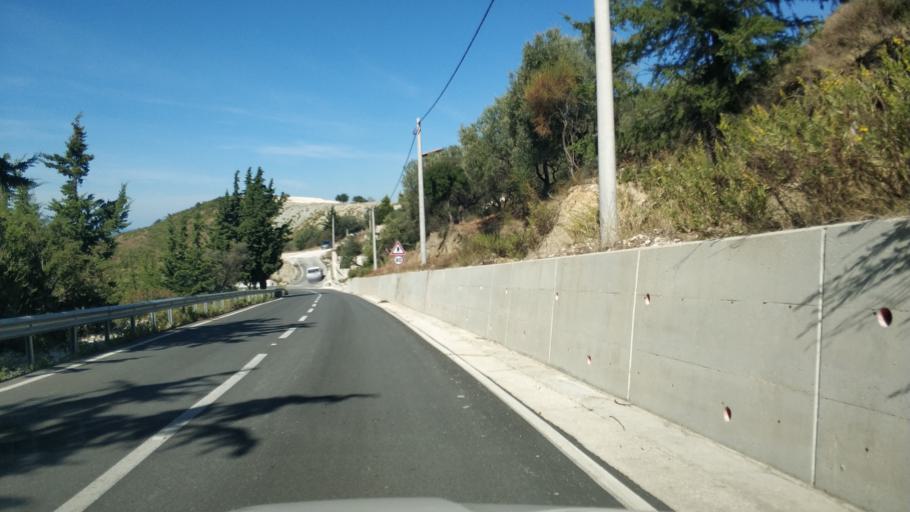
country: AL
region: Vlore
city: Vlore
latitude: 40.4548
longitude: 19.5152
